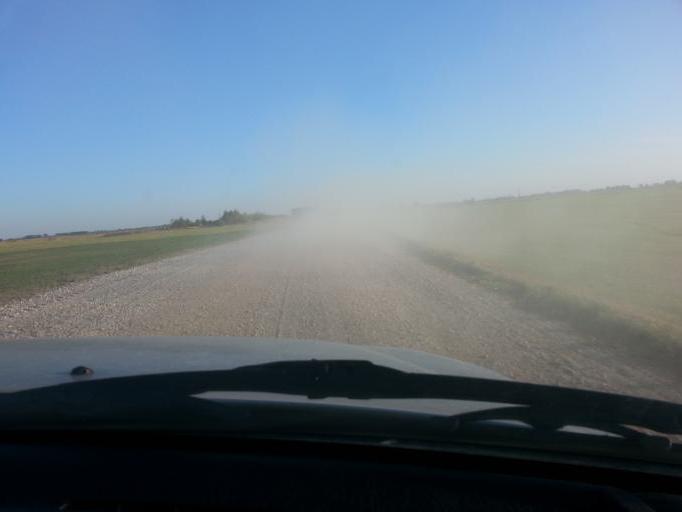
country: LV
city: Tervete
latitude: 56.6167
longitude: 23.4712
